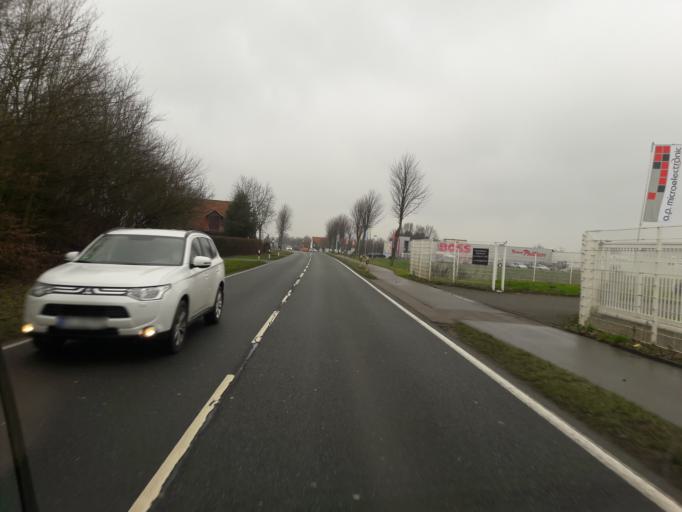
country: DE
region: North Rhine-Westphalia
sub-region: Regierungsbezirk Detmold
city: Minden
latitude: 52.3082
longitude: 8.8444
